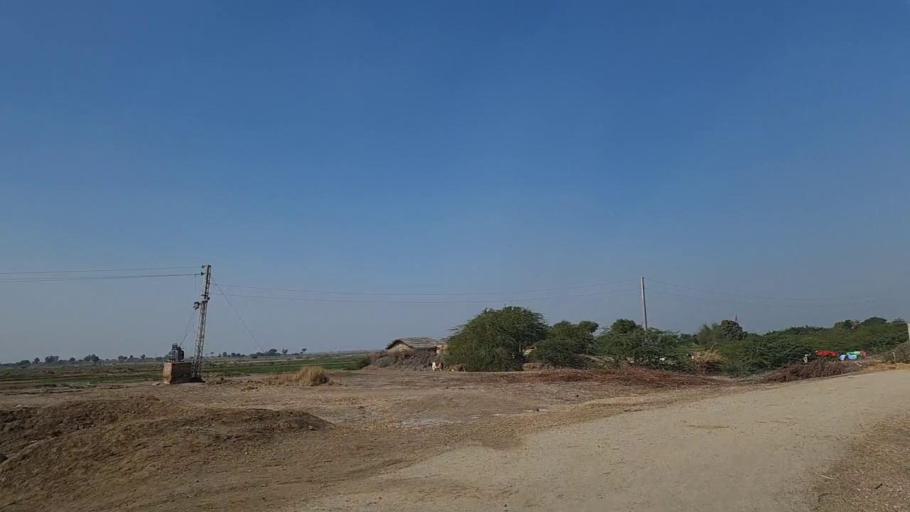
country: PK
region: Sindh
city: Daur
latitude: 26.3549
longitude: 68.3325
